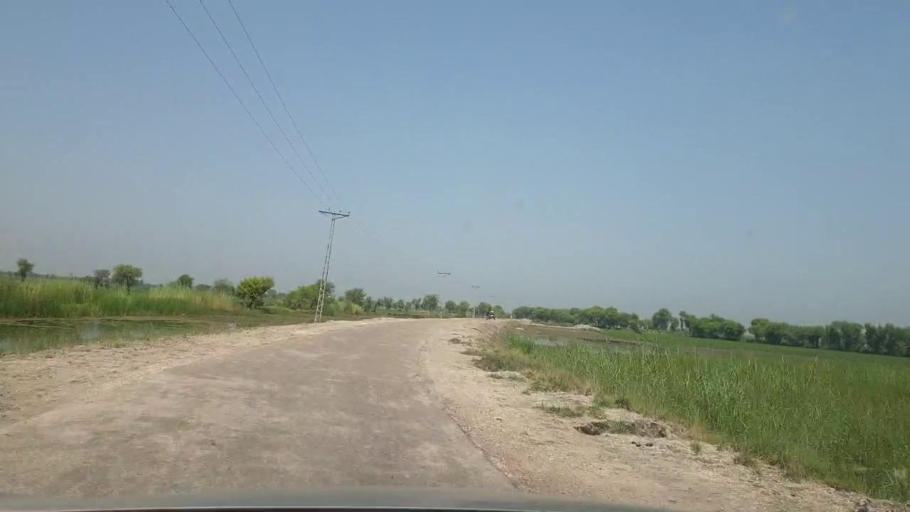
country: PK
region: Sindh
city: Warah
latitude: 27.4680
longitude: 67.7644
